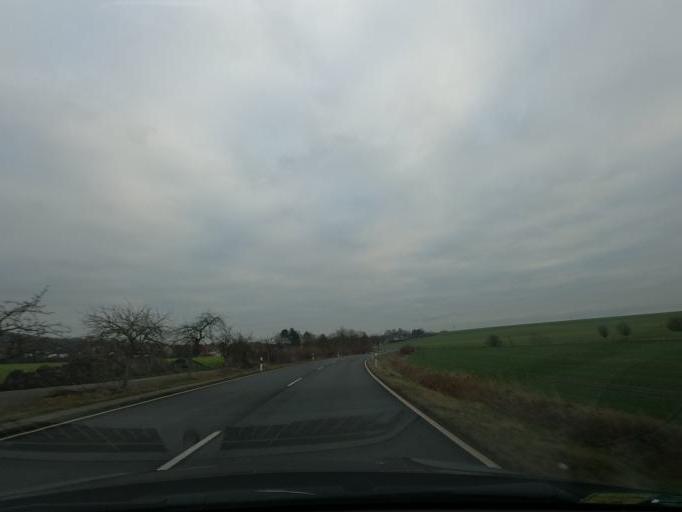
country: DE
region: Lower Saxony
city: Wittmar
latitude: 52.1330
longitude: 10.6349
